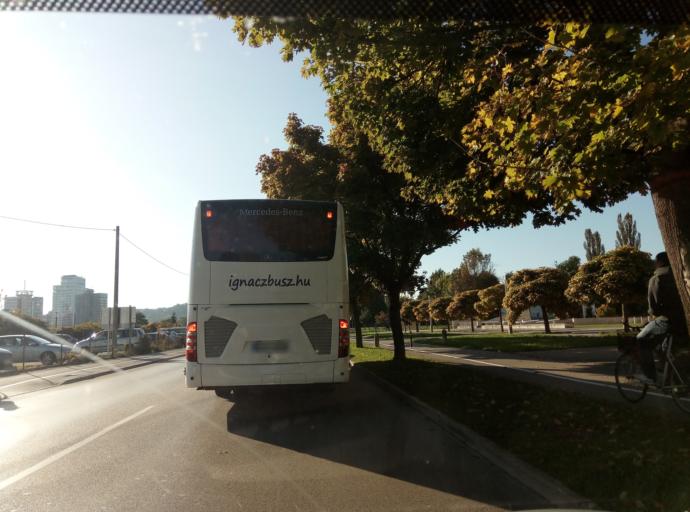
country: SI
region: Ljubljana
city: Ljubljana
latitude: 46.0600
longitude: 14.5144
